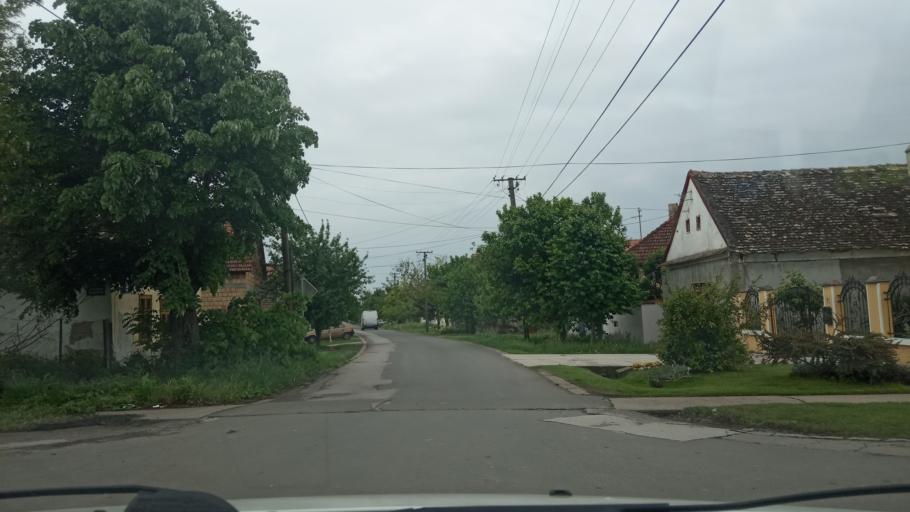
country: RS
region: Autonomna Pokrajina Vojvodina
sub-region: Sremski Okrug
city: Stara Pazova
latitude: 44.9953
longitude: 20.1520
